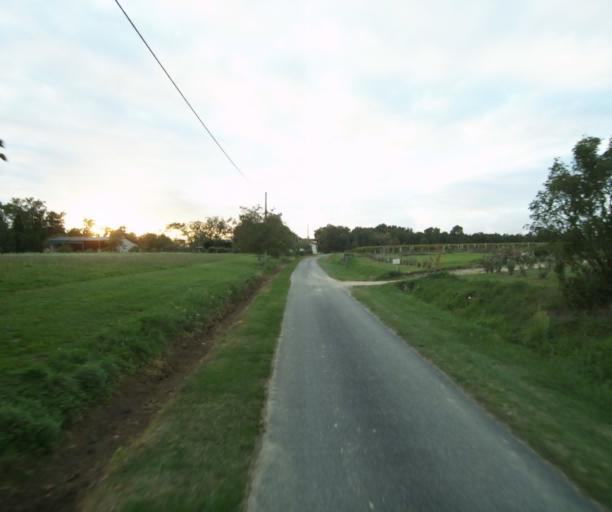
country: FR
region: Aquitaine
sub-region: Departement des Landes
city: Gabarret
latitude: 43.9681
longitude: 0.0973
